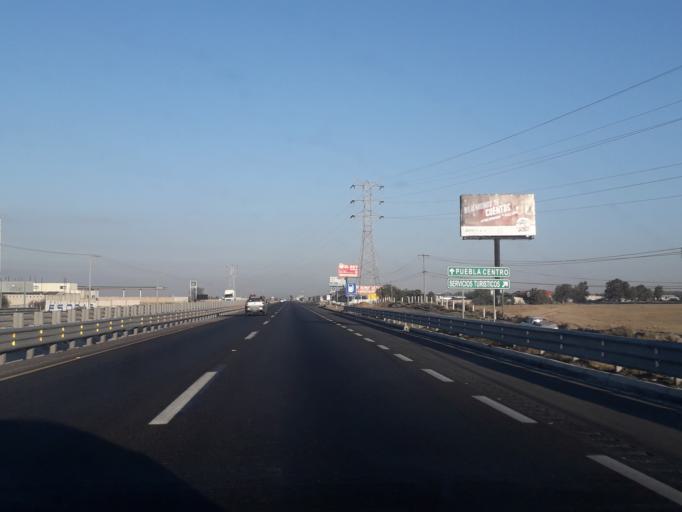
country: MX
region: Puebla
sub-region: Amozoc
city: Amozoc de Mota
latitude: 19.0540
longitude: -98.0488
